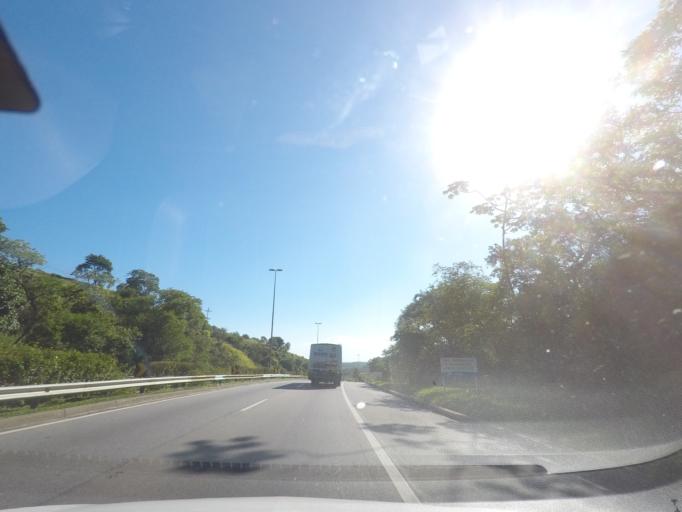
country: BR
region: Rio de Janeiro
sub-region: Sao Goncalo
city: Sao Goncalo
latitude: -22.6637
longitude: -43.0951
